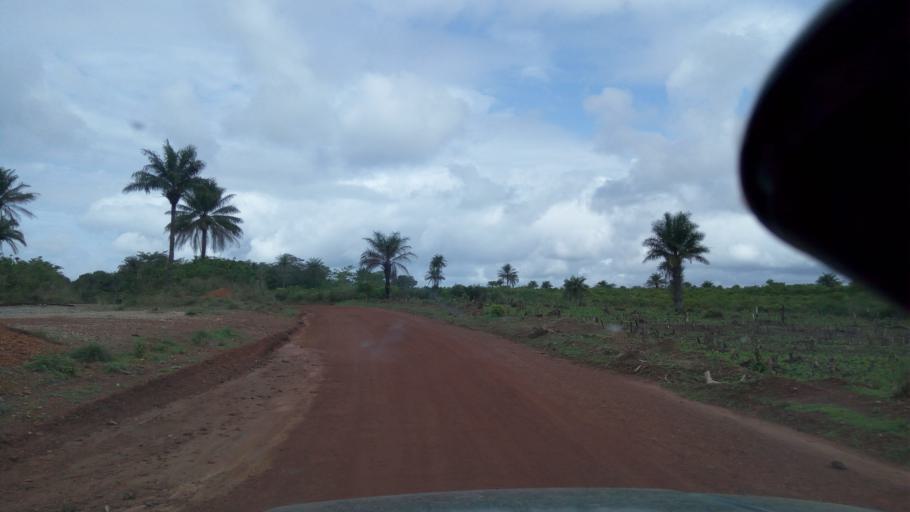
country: SL
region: Northern Province
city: Pepel
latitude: 8.6210
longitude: -13.0407
